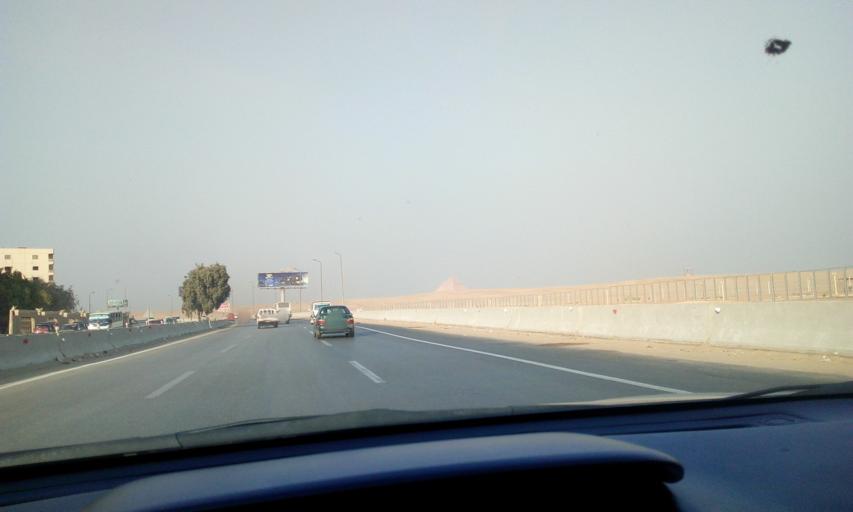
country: EG
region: Al Jizah
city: Al Jizah
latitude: 29.9574
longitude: 31.1071
